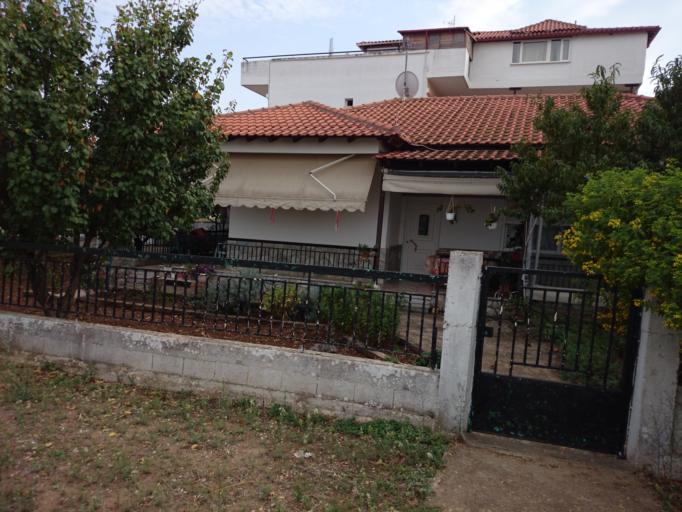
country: GR
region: Central Macedonia
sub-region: Nomos Chalkidikis
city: Nea Moudhania
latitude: 40.2511
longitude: 23.2539
